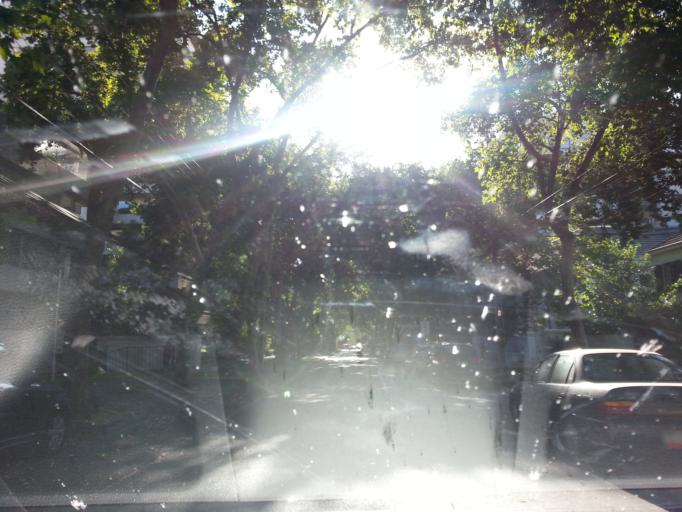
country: CL
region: Santiago Metropolitan
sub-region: Provincia de Santiago
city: Villa Presidente Frei, Nunoa, Santiago, Chile
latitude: -33.4252
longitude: -70.6042
